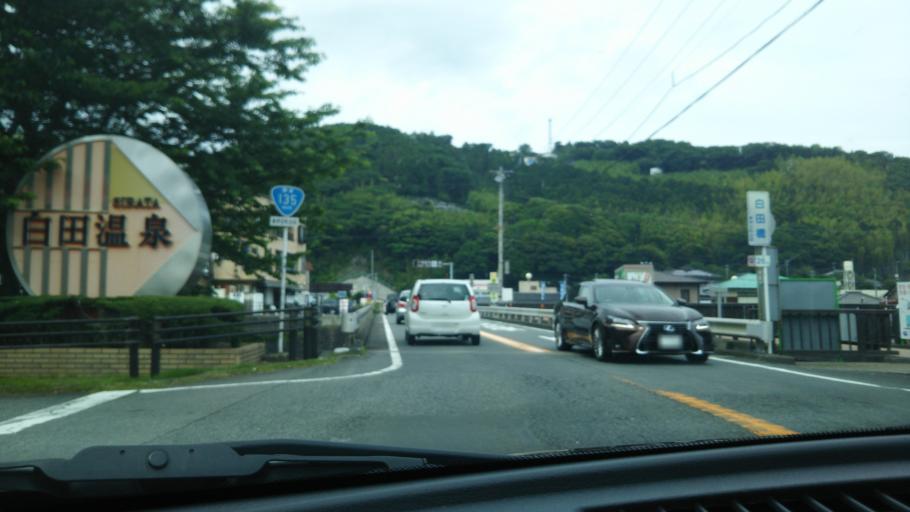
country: JP
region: Shizuoka
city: Ito
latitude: 34.8043
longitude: 139.0584
